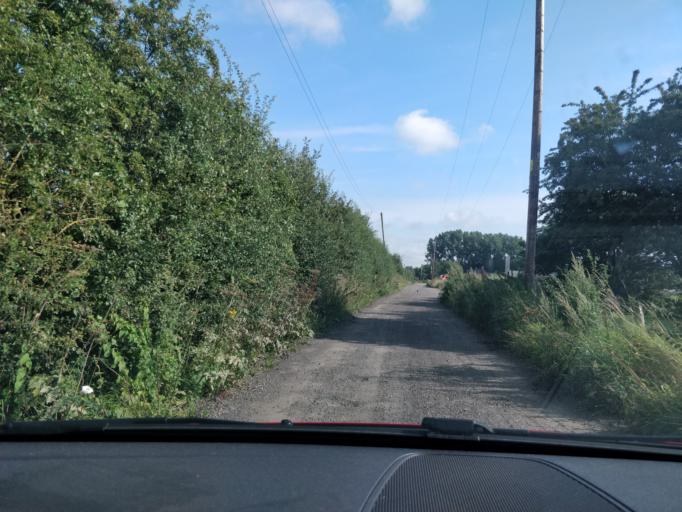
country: GB
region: England
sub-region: Sefton
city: Southport
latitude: 53.6505
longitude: -2.9559
